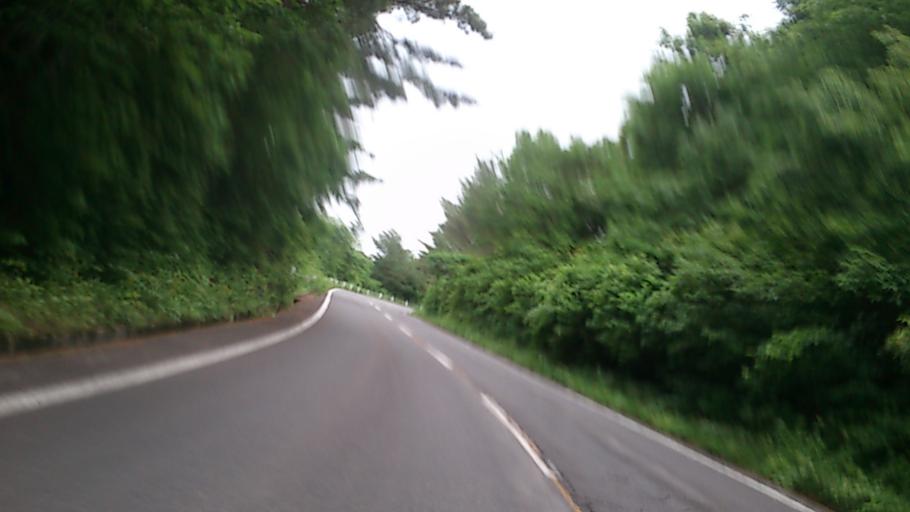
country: JP
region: Yamagata
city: Yuza
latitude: 39.1447
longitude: 139.9672
